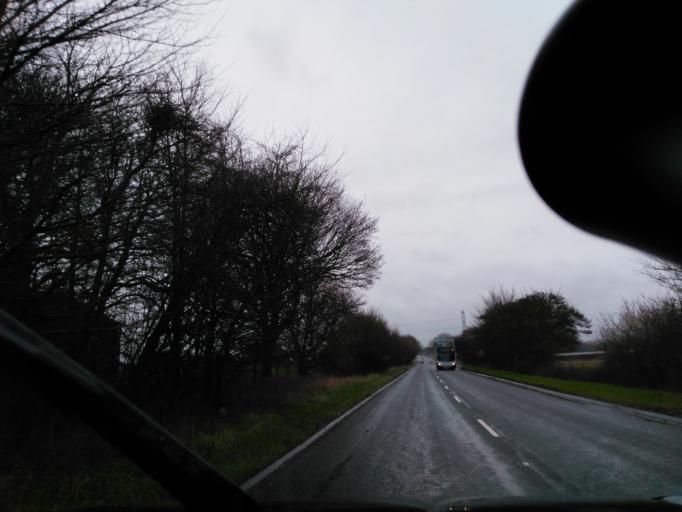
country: GB
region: England
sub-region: Wiltshire
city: Holt
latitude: 51.3362
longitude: -2.1631
